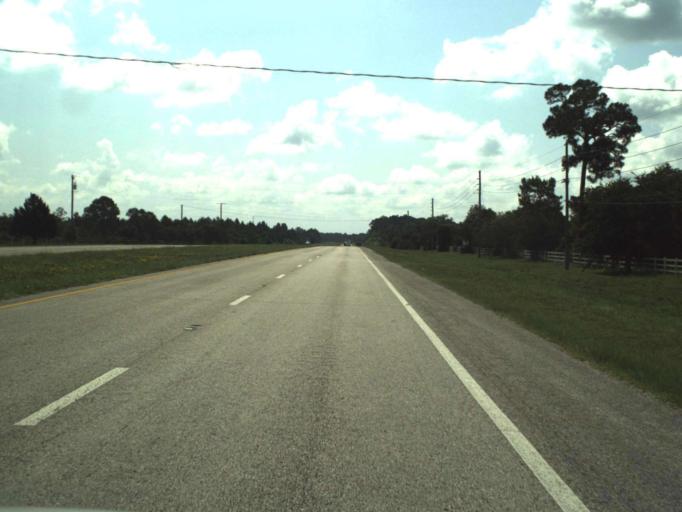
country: US
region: Florida
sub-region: Volusia County
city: Samsula-Spruce Creek
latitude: 29.0170
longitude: -81.0994
